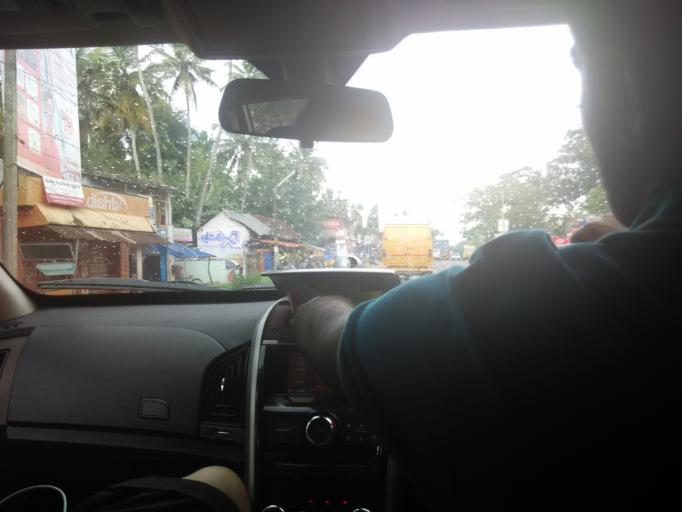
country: IN
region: Kerala
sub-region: Thiruvananthapuram
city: Attingal
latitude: 8.6473
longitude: 76.8422
